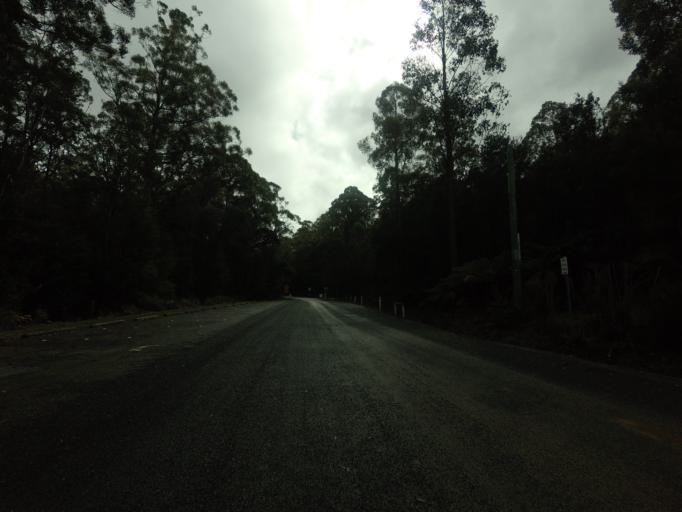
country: AU
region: Tasmania
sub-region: Huon Valley
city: Geeveston
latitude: -43.4125
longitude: 146.8739
